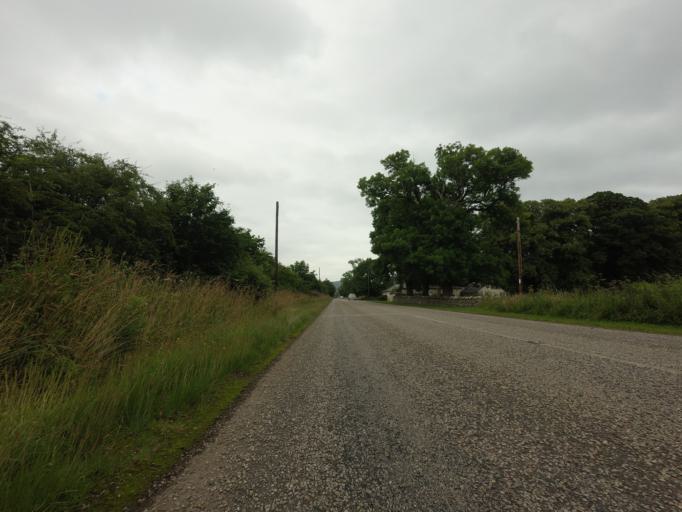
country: GB
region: Scotland
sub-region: Highland
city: Alness
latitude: 57.9133
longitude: -4.3803
